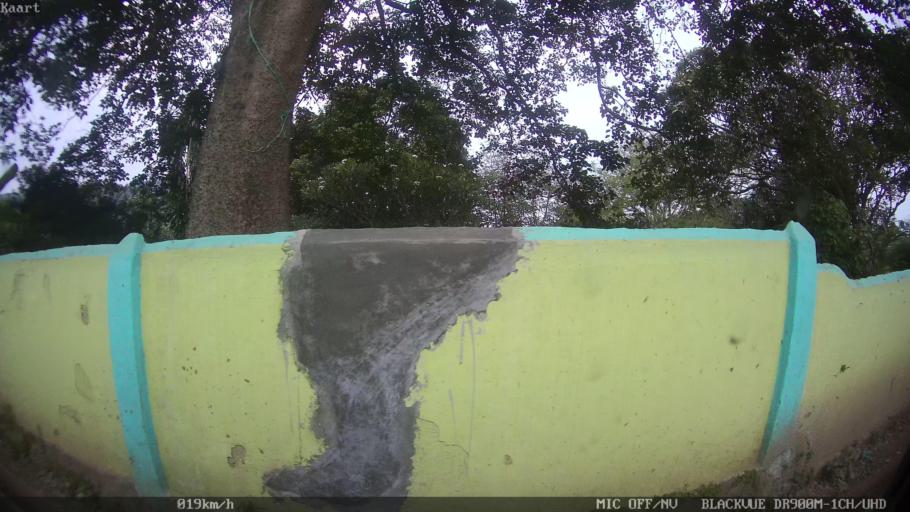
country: ID
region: Lampung
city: Panjang
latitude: -5.4399
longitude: 105.2998
